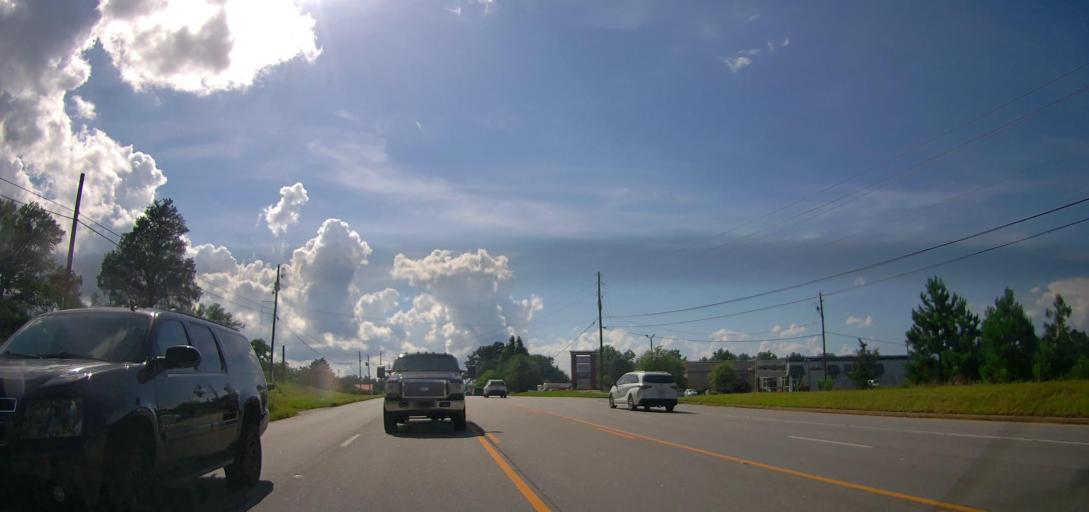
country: US
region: Alabama
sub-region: Russell County
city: Ladonia
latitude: 32.4685
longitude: -85.0798
